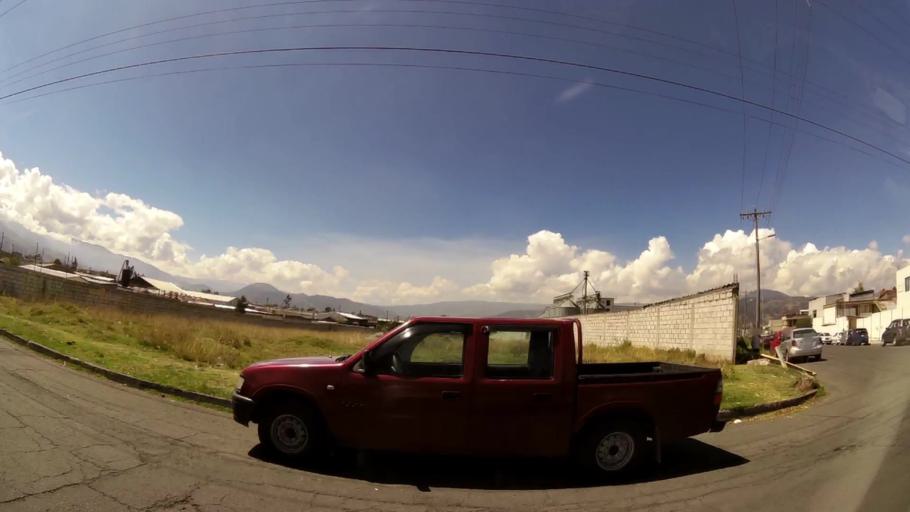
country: EC
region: Chimborazo
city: Riobamba
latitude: -1.6818
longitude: -78.6314
